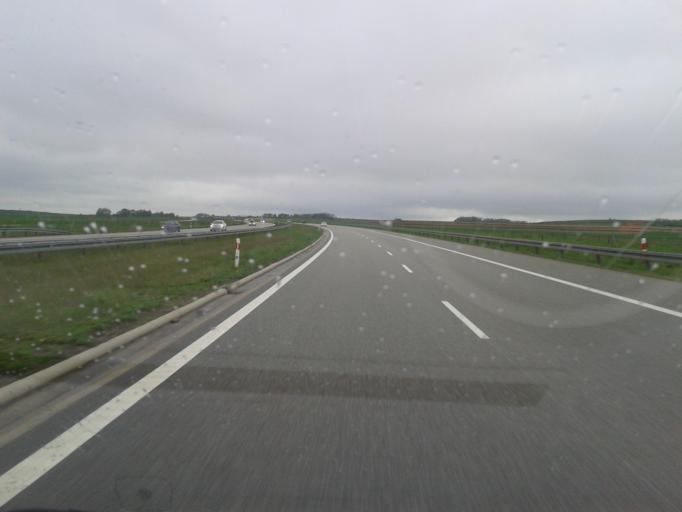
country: PL
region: Subcarpathian Voivodeship
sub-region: Powiat debicki
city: Zyrakow
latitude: 50.0895
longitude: 21.3376
